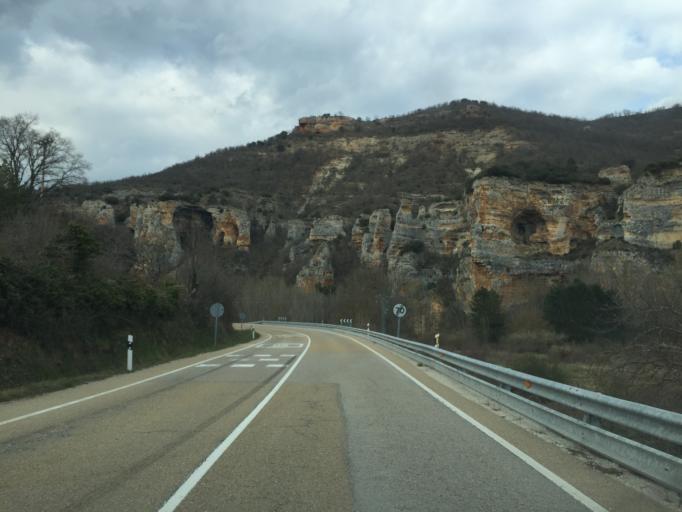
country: ES
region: Castille and Leon
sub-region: Provincia de Burgos
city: Tubilla del Agua
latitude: 42.7371
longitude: -3.8005
